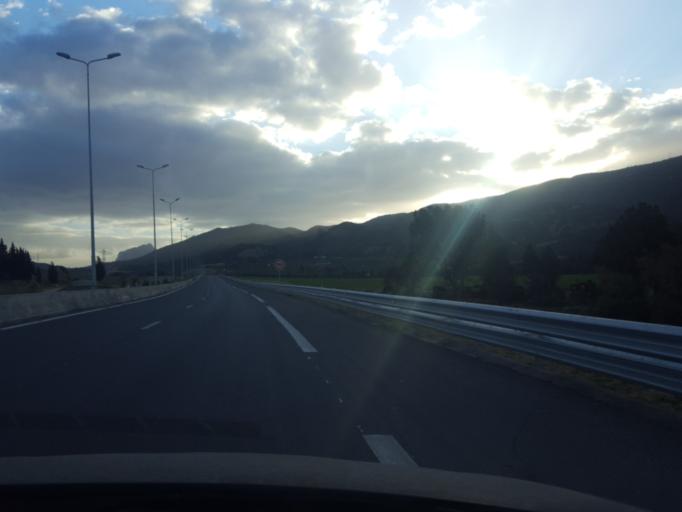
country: TN
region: Tunis
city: Hammam-Lif
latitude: 36.6869
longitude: 10.3884
